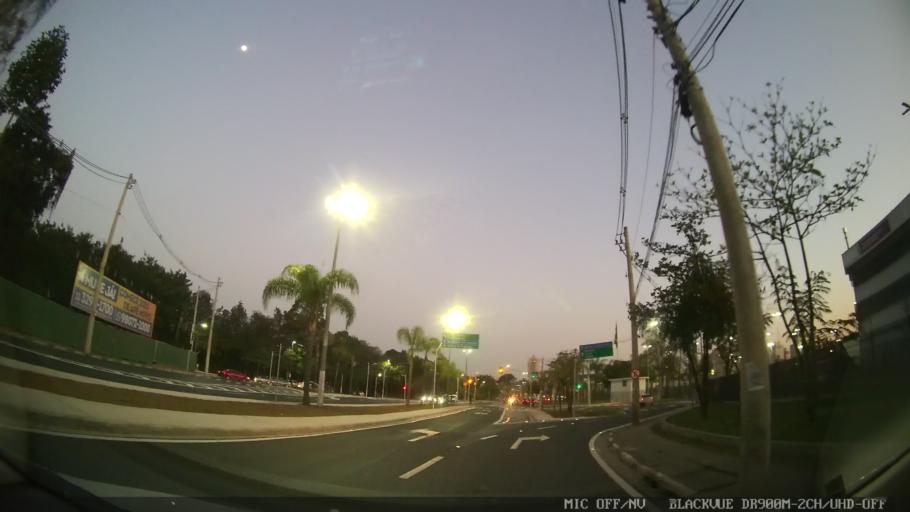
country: BR
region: Sao Paulo
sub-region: Barueri
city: Barueri
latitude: -23.4959
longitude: -46.8676
